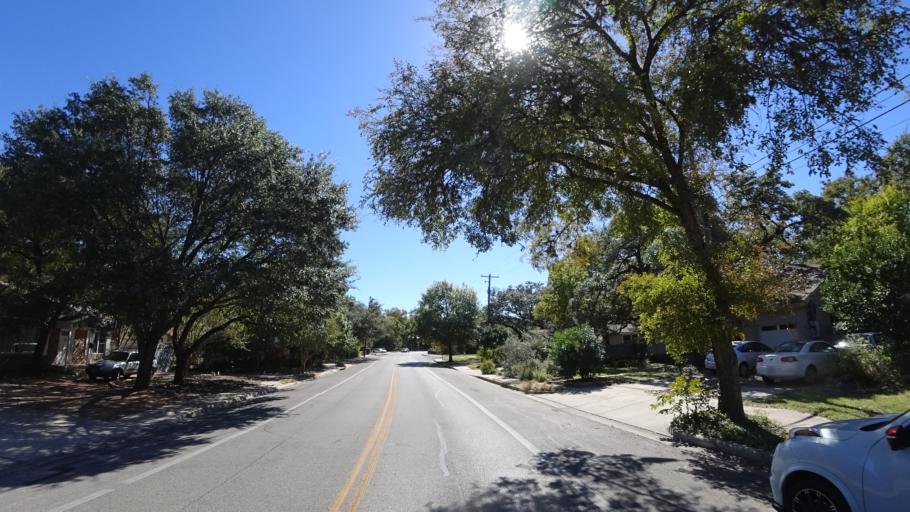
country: US
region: Texas
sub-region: Travis County
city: Austin
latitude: 30.3218
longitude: -97.7447
